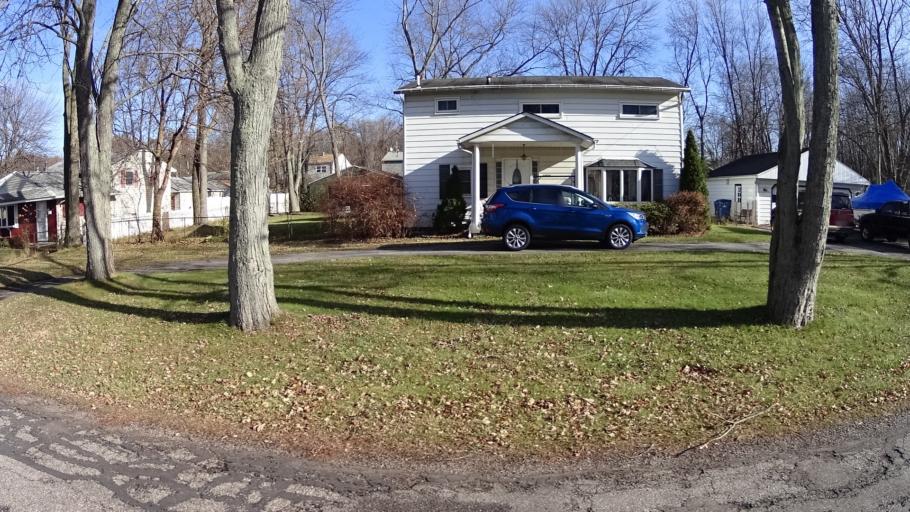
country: US
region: Ohio
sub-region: Lorain County
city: North Ridgeville
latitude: 41.4068
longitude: -81.9869
